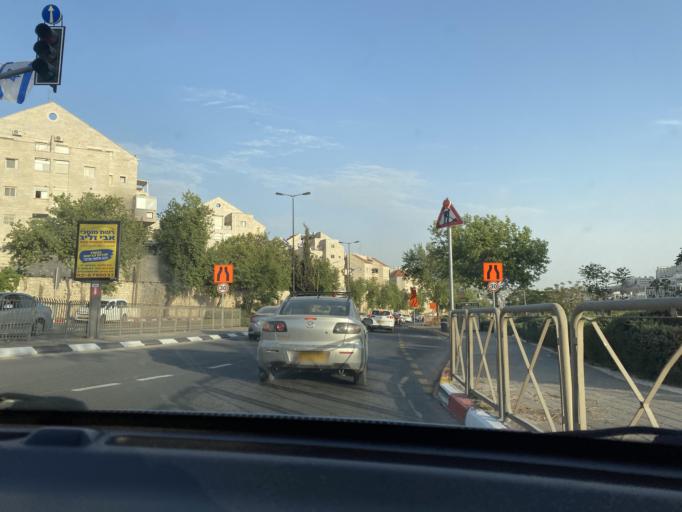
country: IL
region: Jerusalem
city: Jerusalem
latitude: 31.7719
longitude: 35.1886
